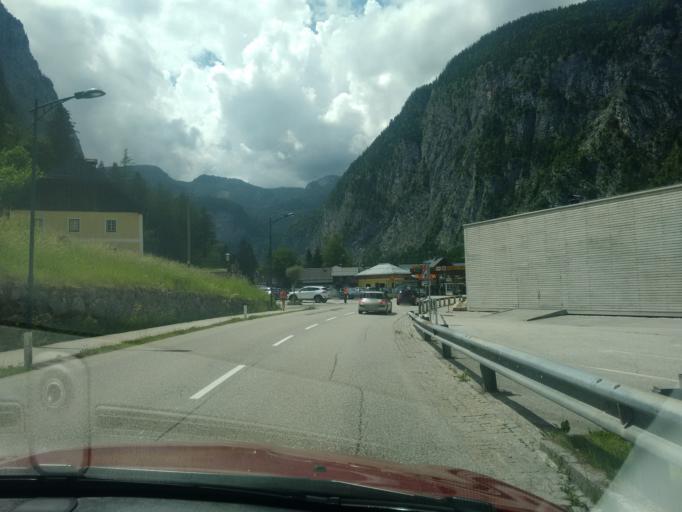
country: AT
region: Upper Austria
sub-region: Politischer Bezirk Gmunden
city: Bad Goisern
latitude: 47.5527
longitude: 13.6492
